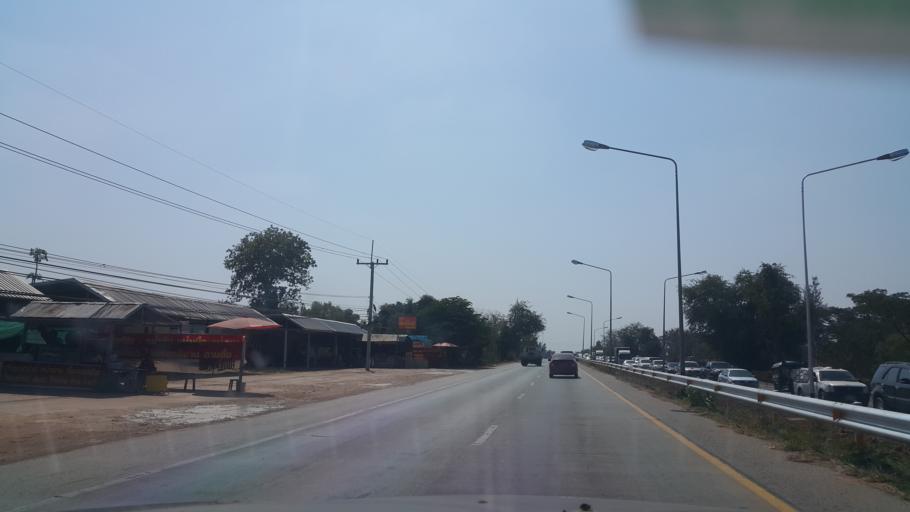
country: TH
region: Khon Kaen
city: Phon
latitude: 15.8860
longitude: 102.6425
